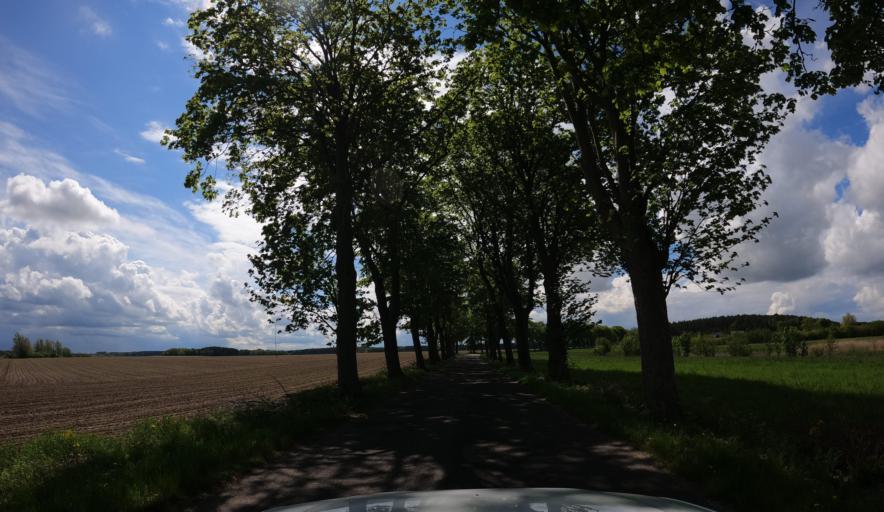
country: PL
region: West Pomeranian Voivodeship
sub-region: Powiat kamienski
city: Wolin
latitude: 53.8939
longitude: 14.6645
